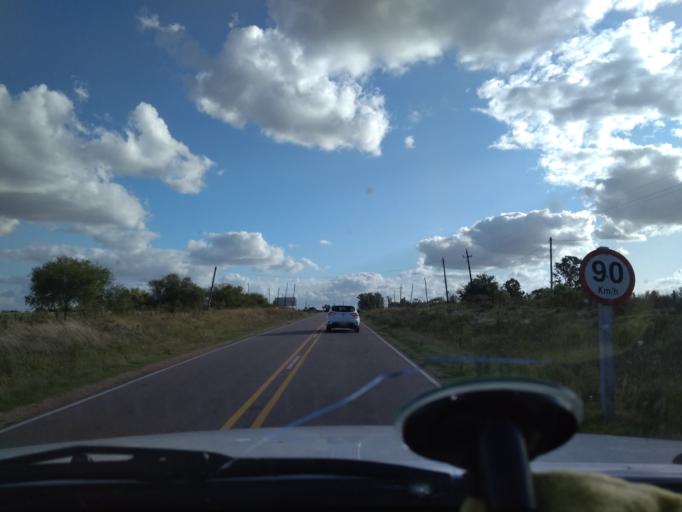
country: UY
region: Canelones
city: Tala
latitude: -34.3672
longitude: -55.7814
